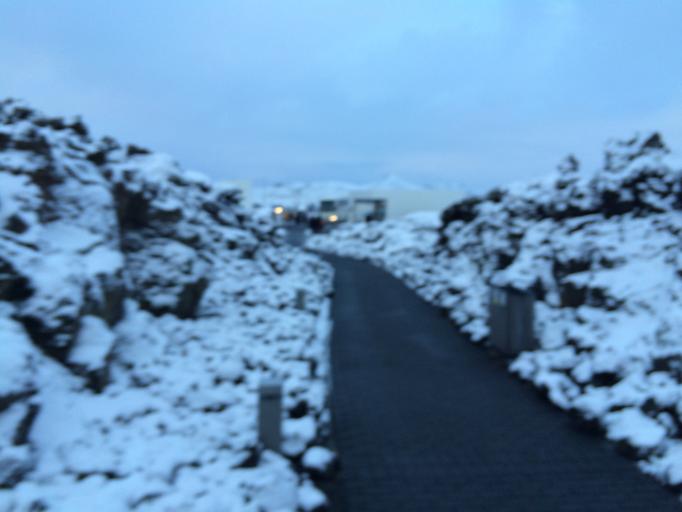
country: IS
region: Southern Peninsula
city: Grindavik
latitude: 63.8813
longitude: -22.4514
